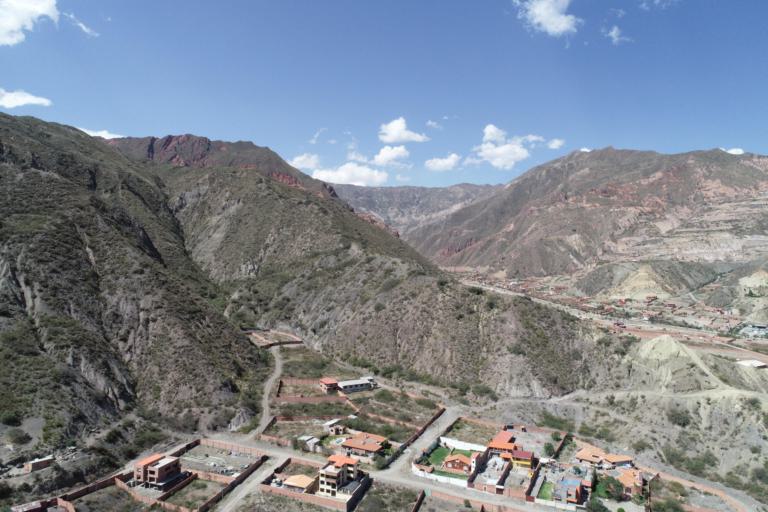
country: BO
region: La Paz
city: La Paz
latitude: -16.6506
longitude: -68.0362
